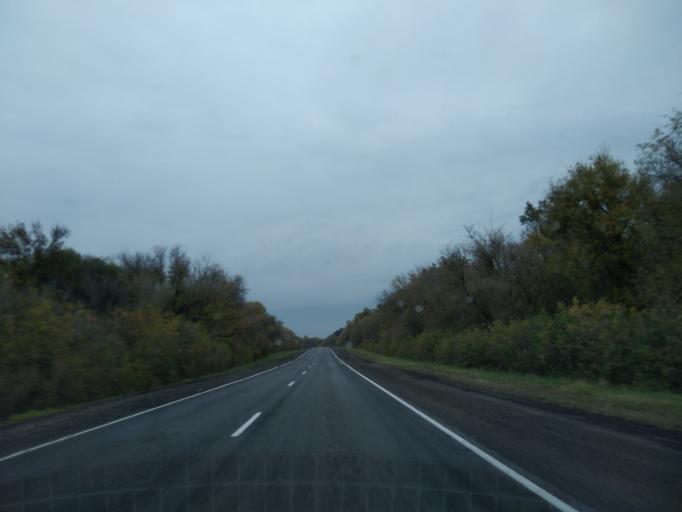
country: RU
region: Lipetsk
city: Zadonsk
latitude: 52.5131
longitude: 38.7579
